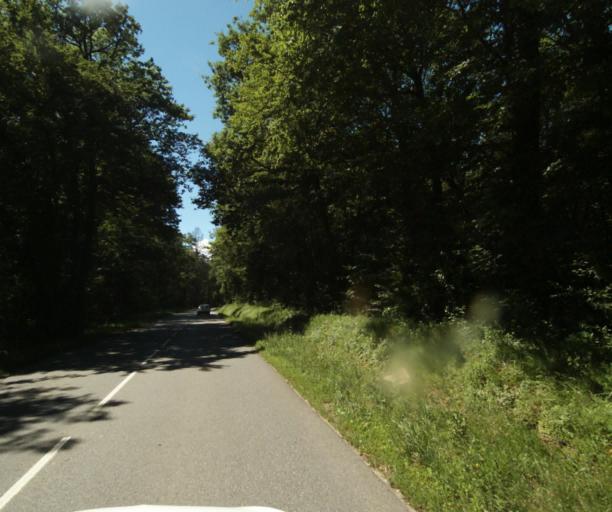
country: FR
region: Rhone-Alpes
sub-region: Departement de la Haute-Savoie
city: Loisin
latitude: 46.2672
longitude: 6.3245
